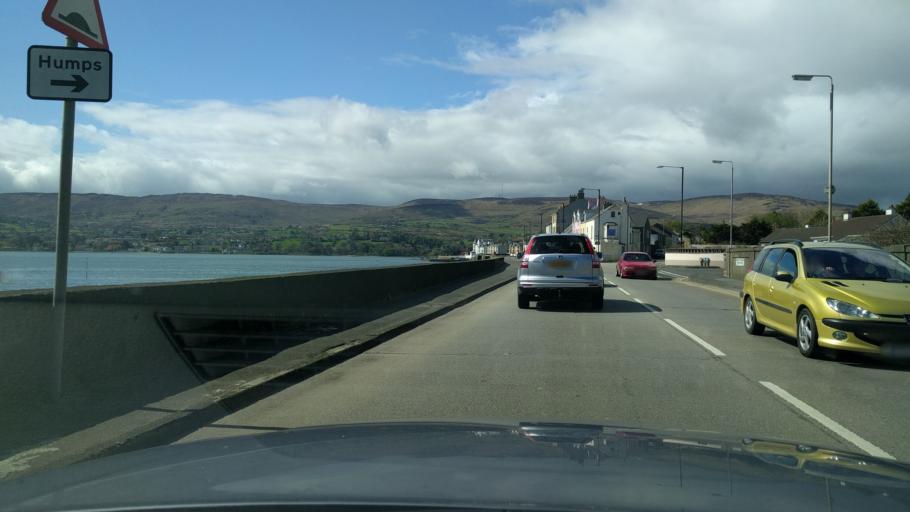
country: GB
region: Northern Ireland
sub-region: Down District
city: Warrenpoint
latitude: 54.1008
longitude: -6.2404
